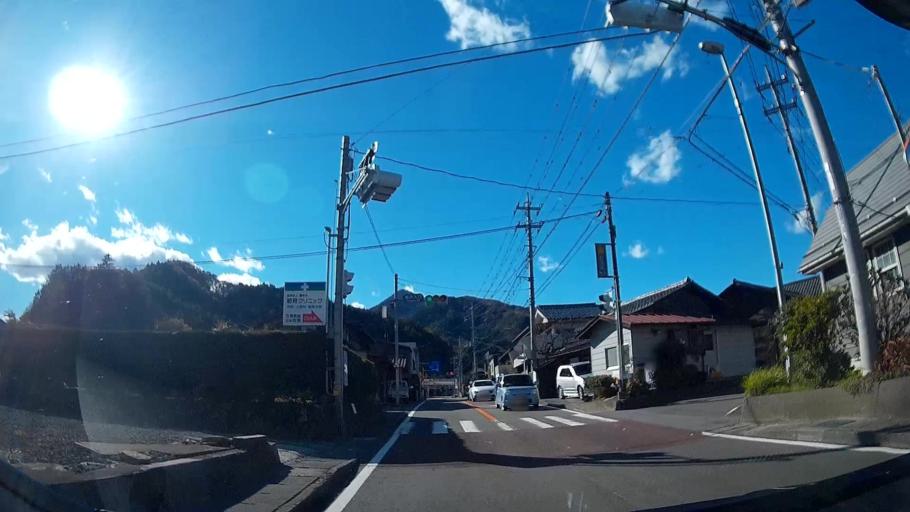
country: JP
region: Yamanashi
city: Otsuki
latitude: 35.5963
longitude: 138.8815
